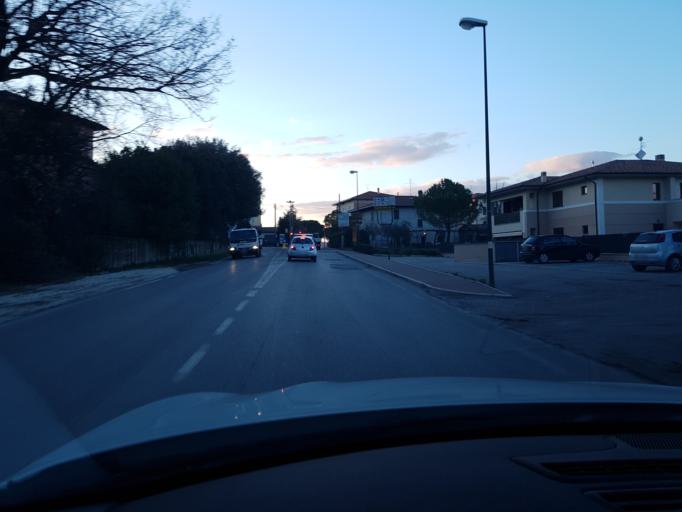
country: IT
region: Umbria
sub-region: Provincia di Perugia
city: Torgiano
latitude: 43.0285
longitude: 12.4416
